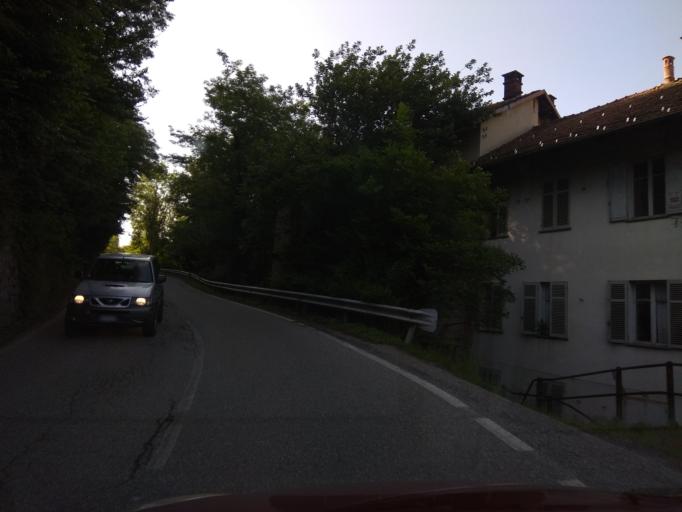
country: IT
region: Piedmont
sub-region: Provincia di Biella
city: Valle Mosso
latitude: 45.6376
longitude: 8.1469
